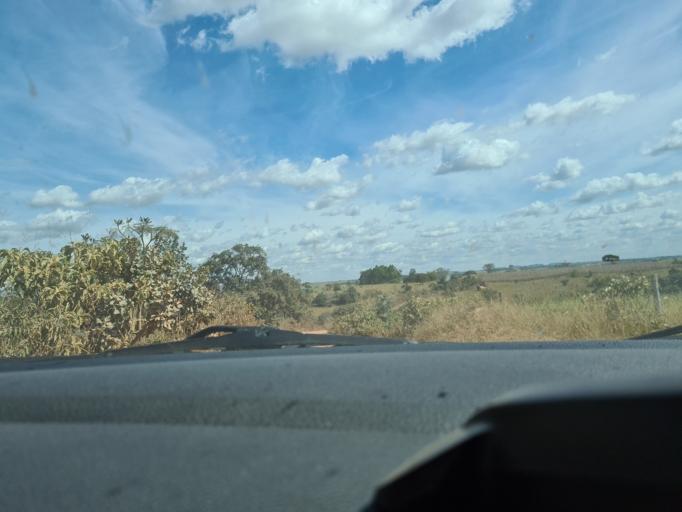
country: BR
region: Goias
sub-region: Silvania
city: Silvania
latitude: -16.5415
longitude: -48.5751
